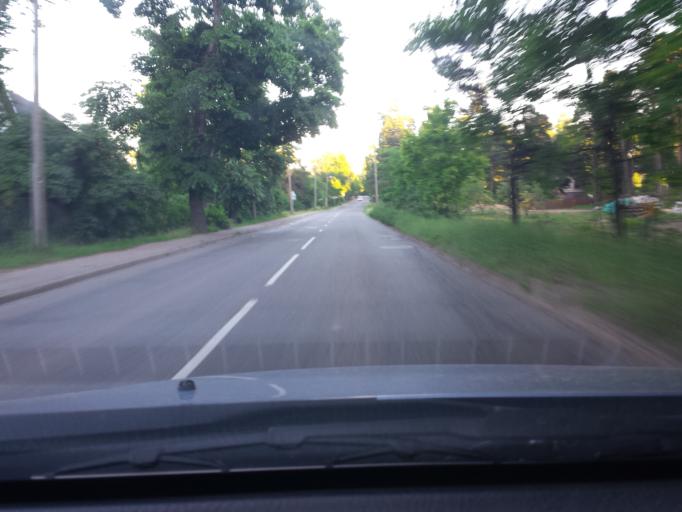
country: LV
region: Riga
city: Jaunciems
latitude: 57.0413
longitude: 24.1737
